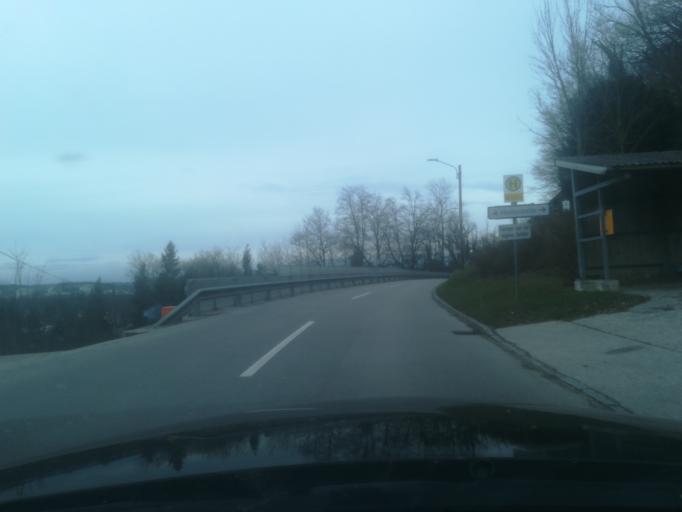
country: AT
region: Upper Austria
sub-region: Wels-Land
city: Steinhaus
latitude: 48.1357
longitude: 14.0085
